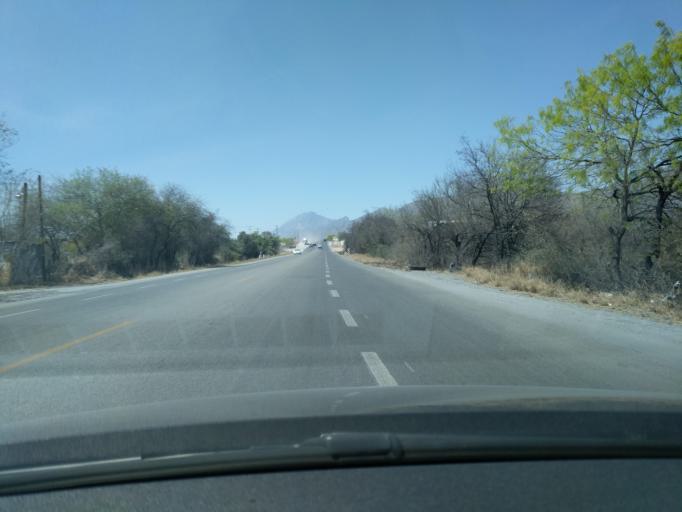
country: MX
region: Nuevo Leon
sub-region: Salinas Victoria
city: Las Torres
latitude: 25.9185
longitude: -100.3670
